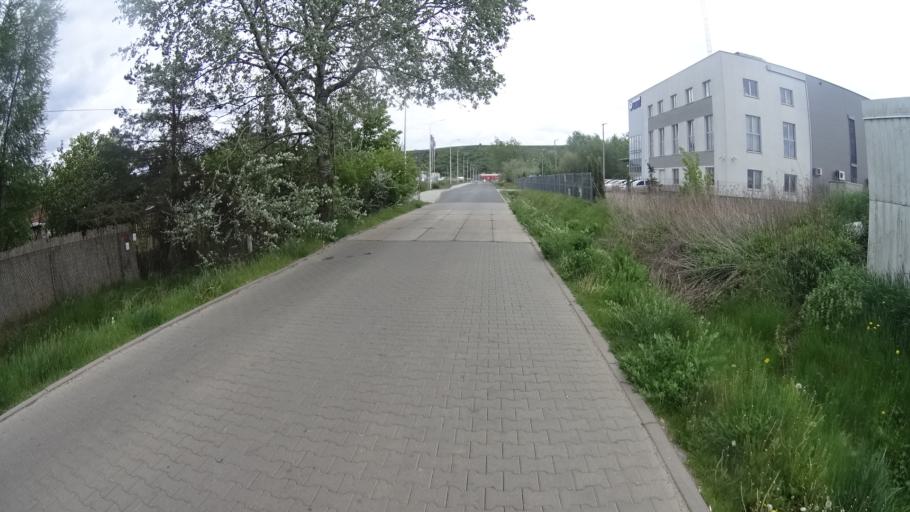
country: PL
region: Masovian Voivodeship
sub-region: Powiat warszawski zachodni
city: Babice
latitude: 52.2775
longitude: 20.8689
